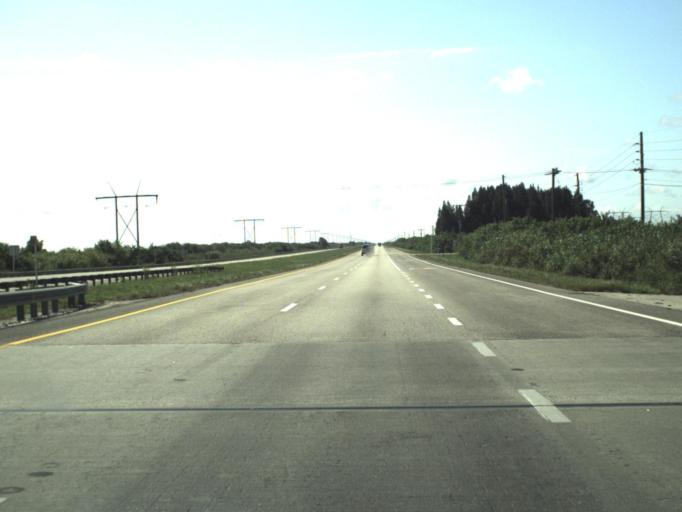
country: US
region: Florida
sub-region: Broward County
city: Weston
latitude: 26.3357
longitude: -80.5387
